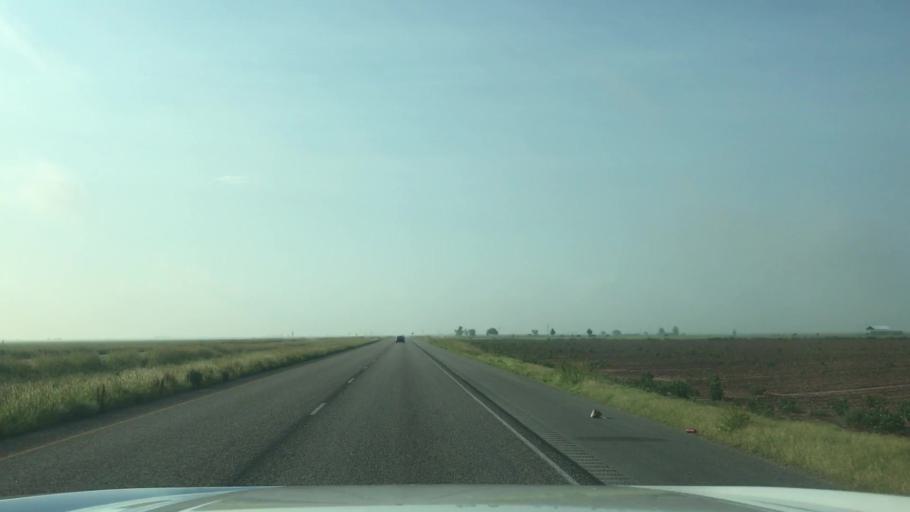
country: US
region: Texas
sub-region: Lubbock County
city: Slaton
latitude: 33.3403
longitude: -101.5414
